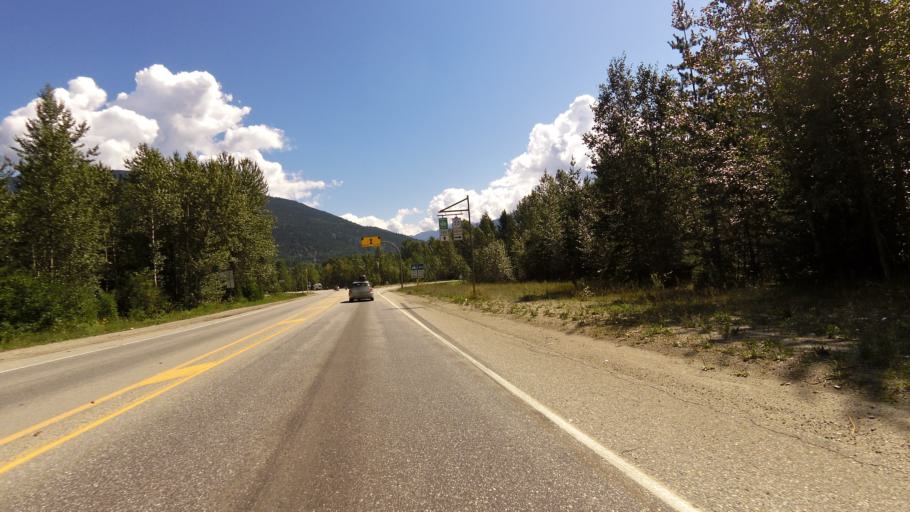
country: CA
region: British Columbia
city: Revelstoke
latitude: 51.0030
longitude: -118.2279
